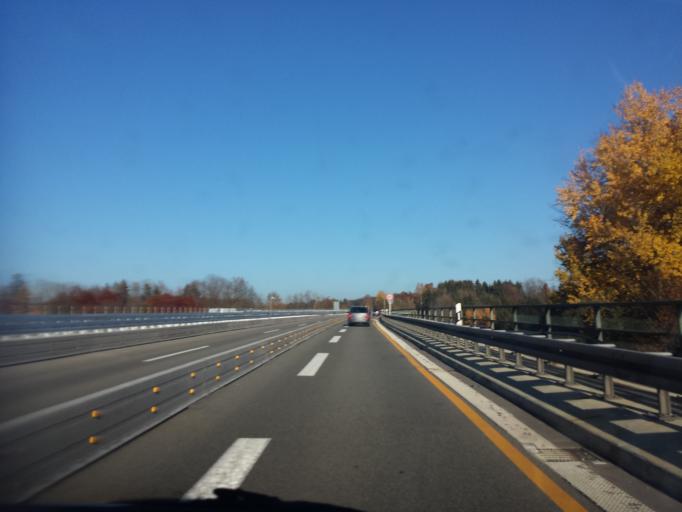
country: DE
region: Bavaria
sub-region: Upper Bavaria
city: Ohlstadt
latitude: 47.6603
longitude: 11.2407
